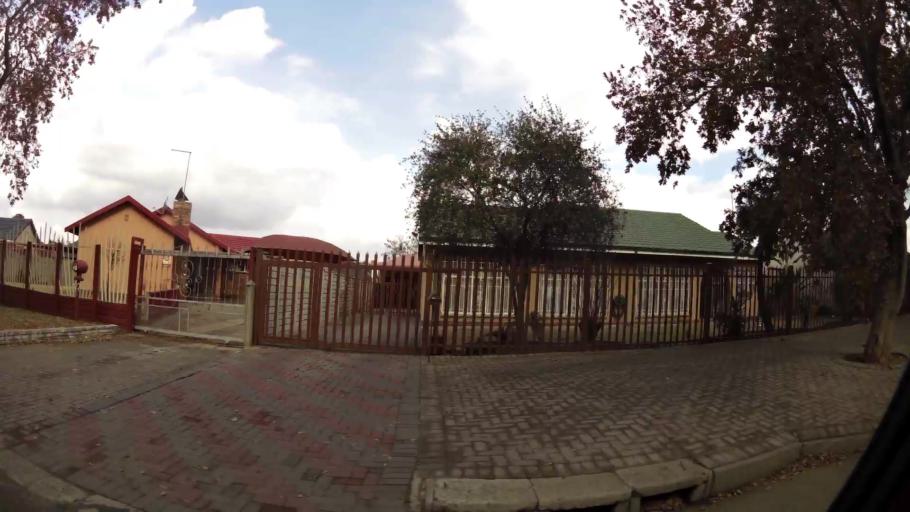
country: ZA
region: Gauteng
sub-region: Sedibeng District Municipality
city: Vanderbijlpark
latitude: -26.7250
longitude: 27.8485
